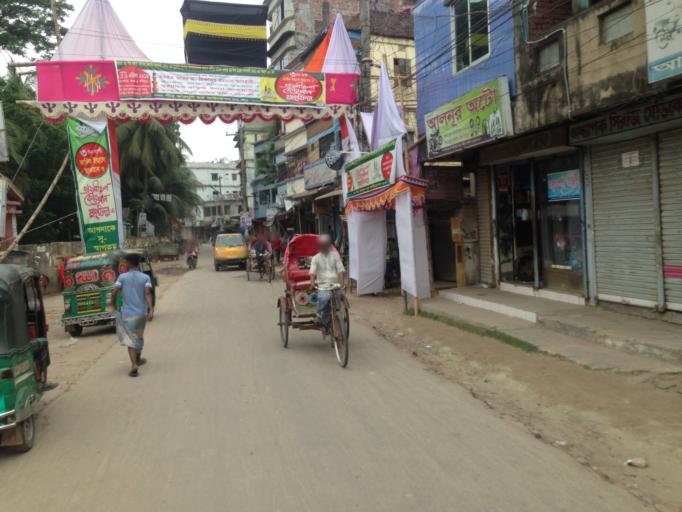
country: BD
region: Chittagong
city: Raipur
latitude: 23.0369
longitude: 90.7640
